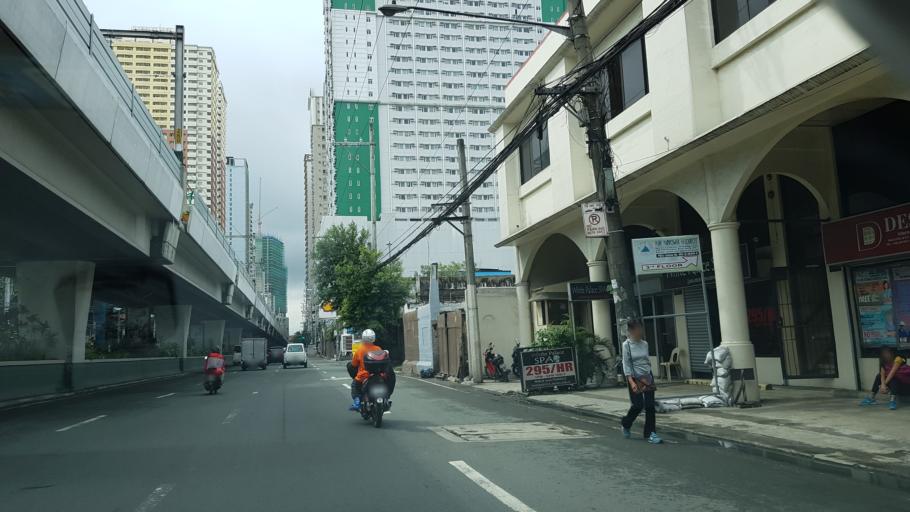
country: PH
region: Metro Manila
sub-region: City of Manila
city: Port Area
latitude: 14.5692
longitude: 120.9920
